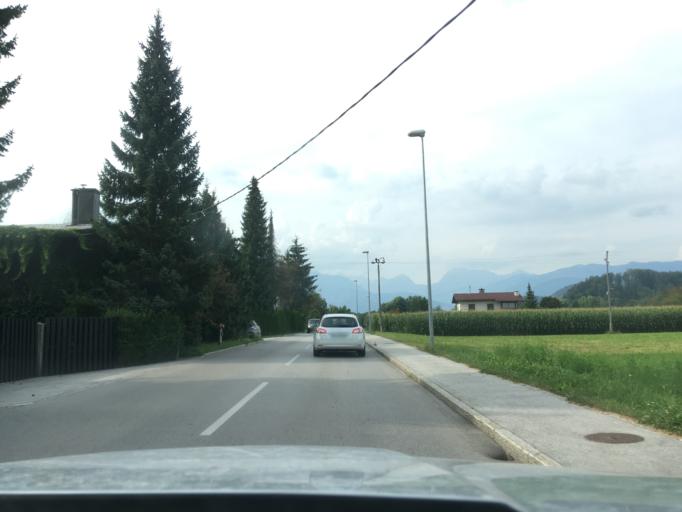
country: SI
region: Domzale
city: Radomlje
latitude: 46.1792
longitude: 14.6092
